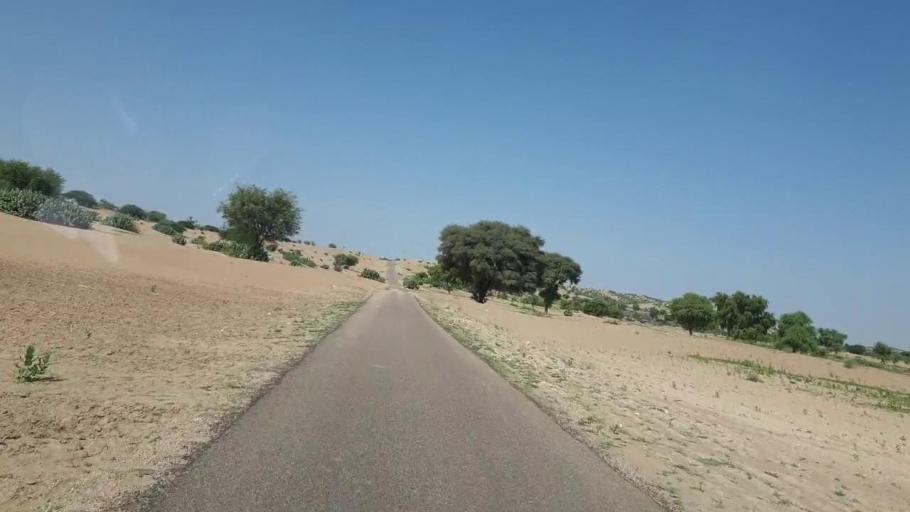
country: PK
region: Sindh
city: Chor
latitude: 25.6108
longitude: 70.3166
